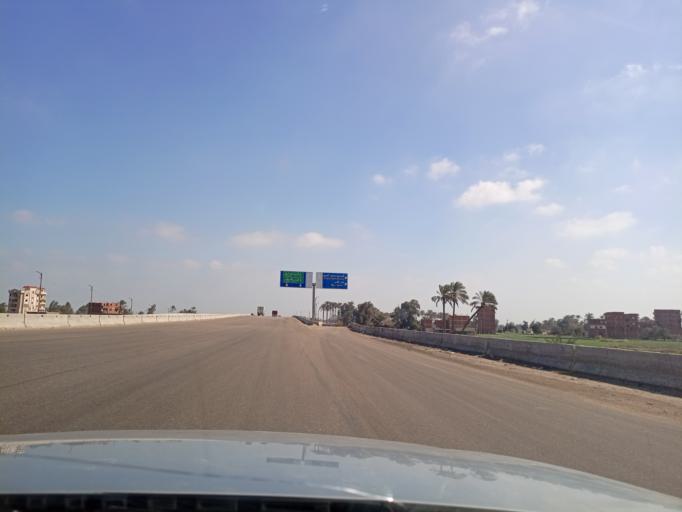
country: EG
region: Eastern Province
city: Mashtul as Suq
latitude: 30.4618
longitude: 31.3633
